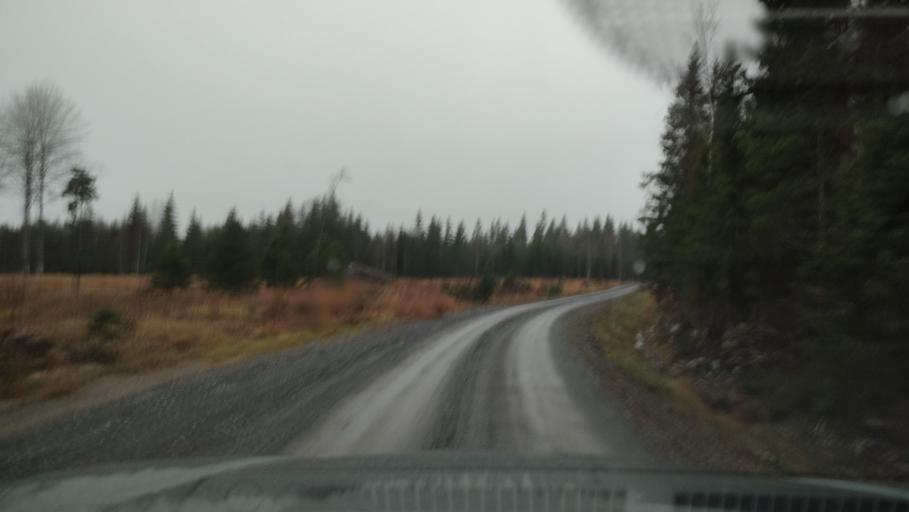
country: FI
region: Southern Ostrobothnia
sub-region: Suupohja
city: Karijoki
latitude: 62.1796
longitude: 21.6923
